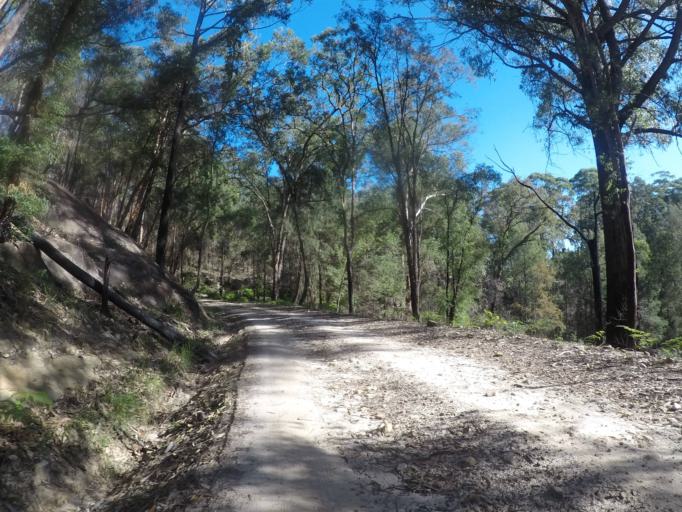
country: AU
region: New South Wales
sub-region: Hornsby Shire
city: Glenorie
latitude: -33.3343
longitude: 151.0746
